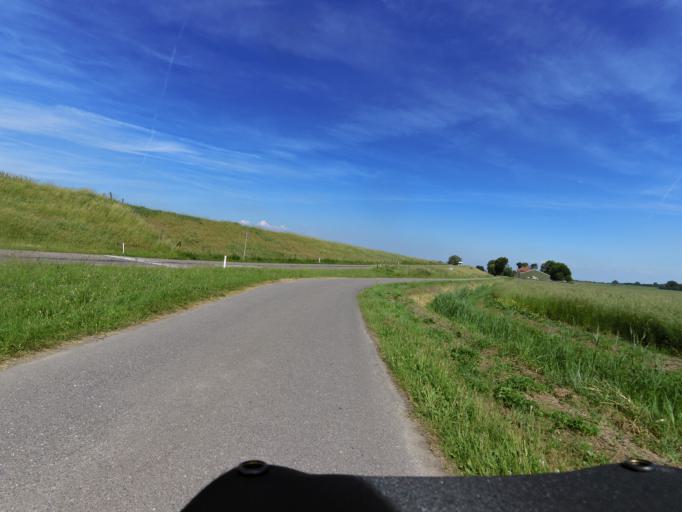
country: NL
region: North Brabant
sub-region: Gemeente Moerdijk
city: Willemstad
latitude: 51.6776
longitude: 4.4053
